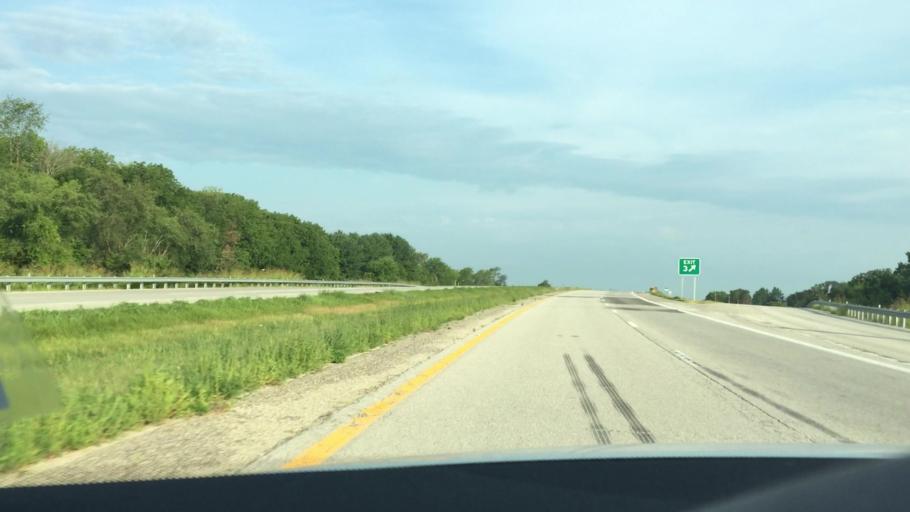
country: US
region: Missouri
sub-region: Buchanan County
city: Saint Joseph
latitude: 39.7198
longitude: -94.8301
